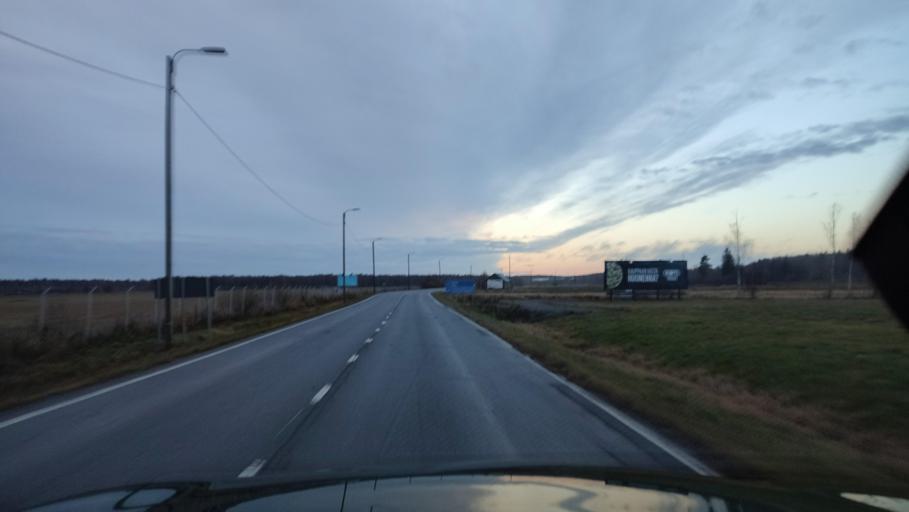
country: FI
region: Ostrobothnia
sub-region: Vaasa
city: Ristinummi
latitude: 63.0435
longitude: 21.7562
